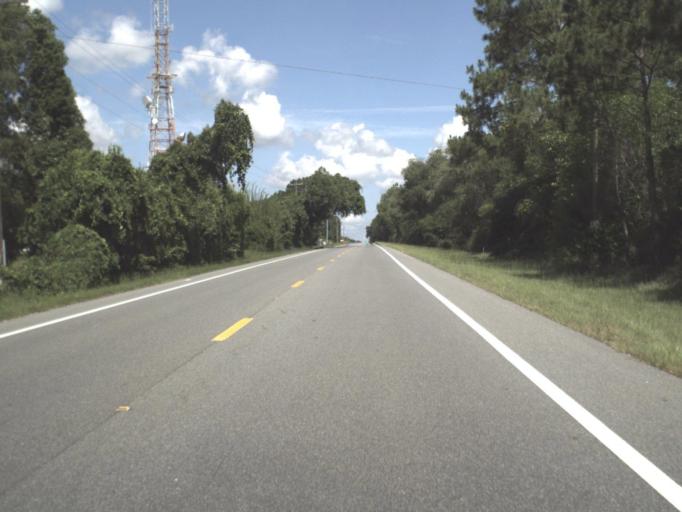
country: US
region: Florida
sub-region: Putnam County
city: Interlachen
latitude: 29.7197
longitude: -81.8172
